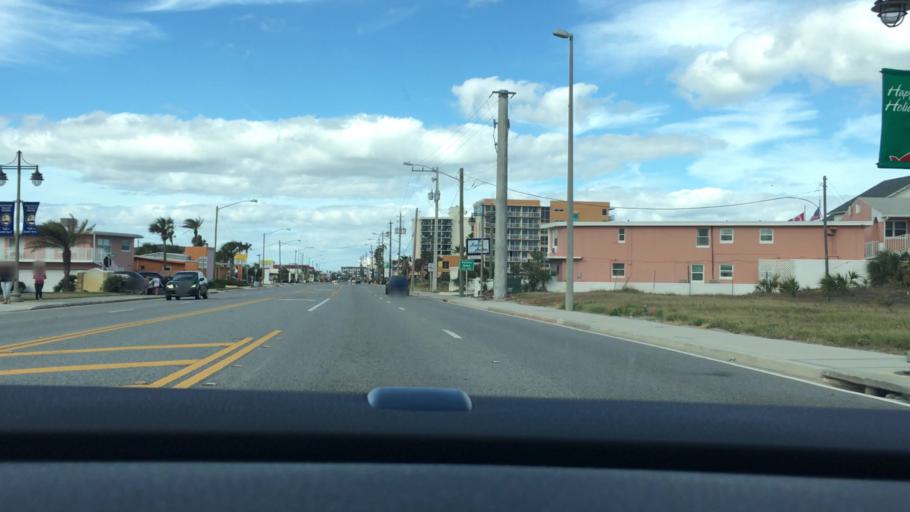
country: US
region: Florida
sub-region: Volusia County
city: Daytona Beach
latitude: 29.2051
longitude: -80.9974
